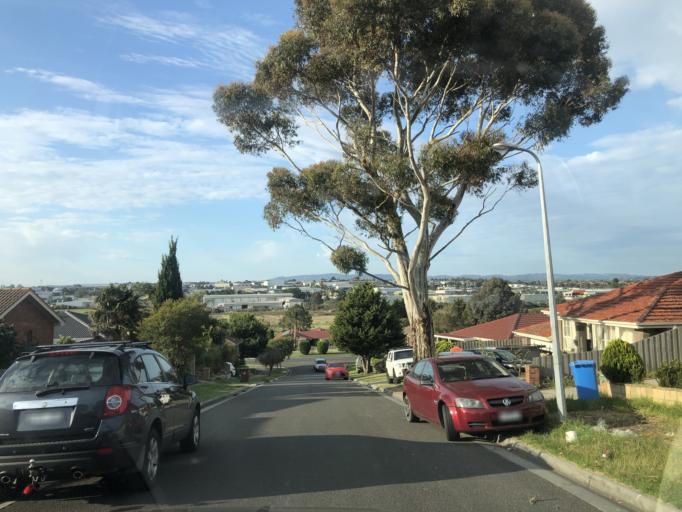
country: AU
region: Victoria
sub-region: Casey
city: Hallam
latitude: -38.0230
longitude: 145.2656
